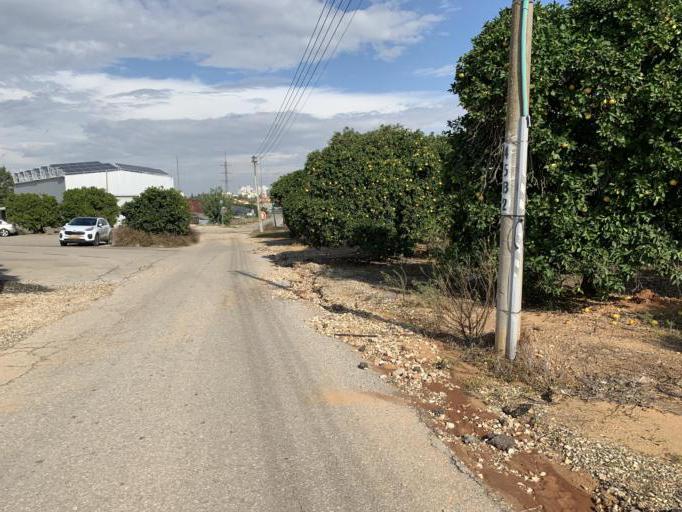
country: IL
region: Central District
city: Ra'anana
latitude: 32.1688
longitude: 34.8776
